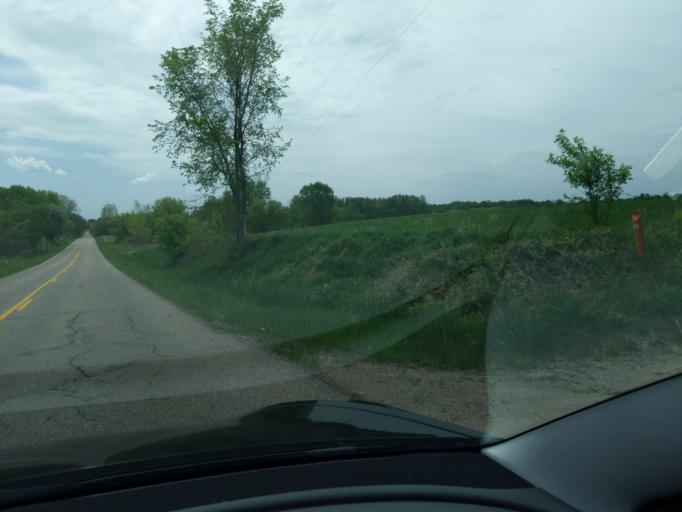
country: US
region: Michigan
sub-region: Ingham County
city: Holt
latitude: 42.5815
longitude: -84.5426
